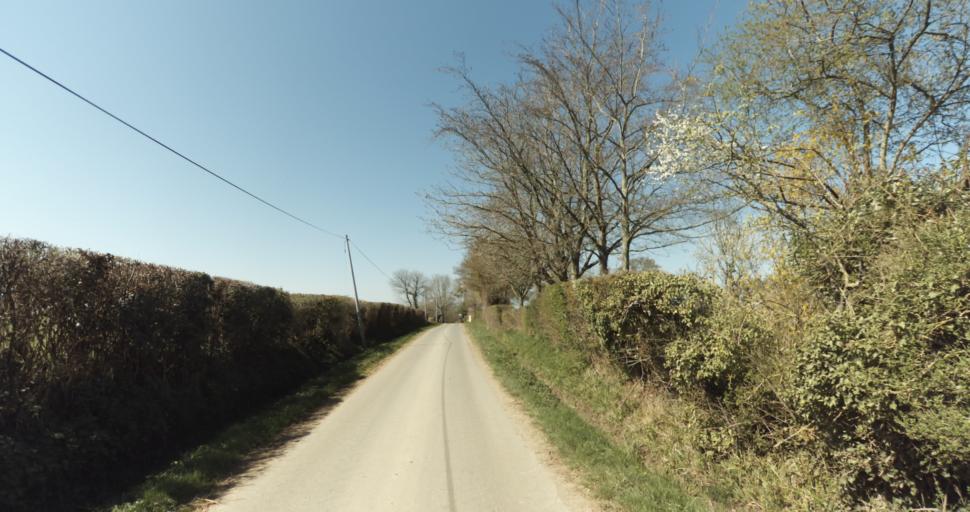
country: FR
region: Lower Normandy
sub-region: Departement du Calvados
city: Saint-Pierre-sur-Dives
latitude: 49.0129
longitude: -0.0043
